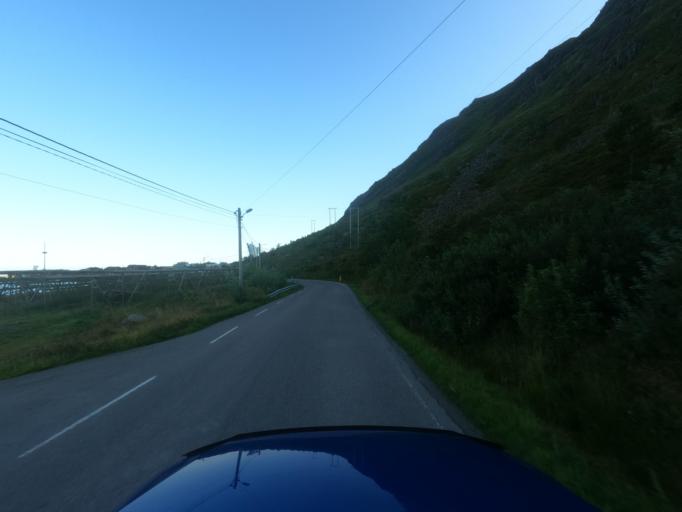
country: NO
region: Nordland
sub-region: Vestvagoy
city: Gravdal
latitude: 68.0725
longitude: 13.5287
